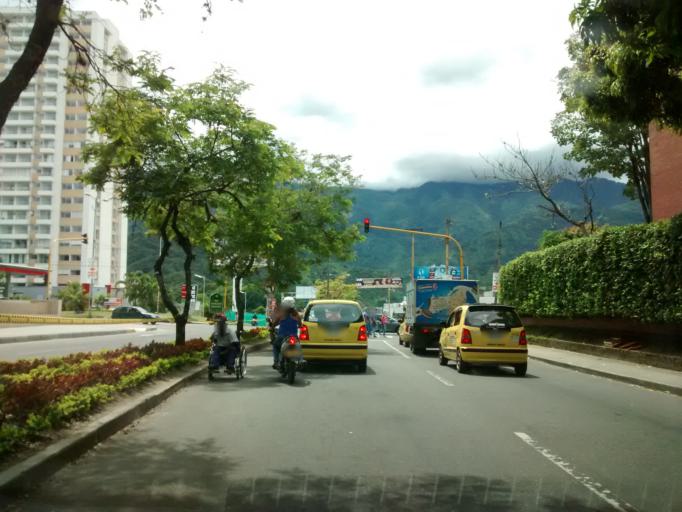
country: CO
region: Tolima
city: Ibague
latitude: 4.4408
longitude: -75.2043
